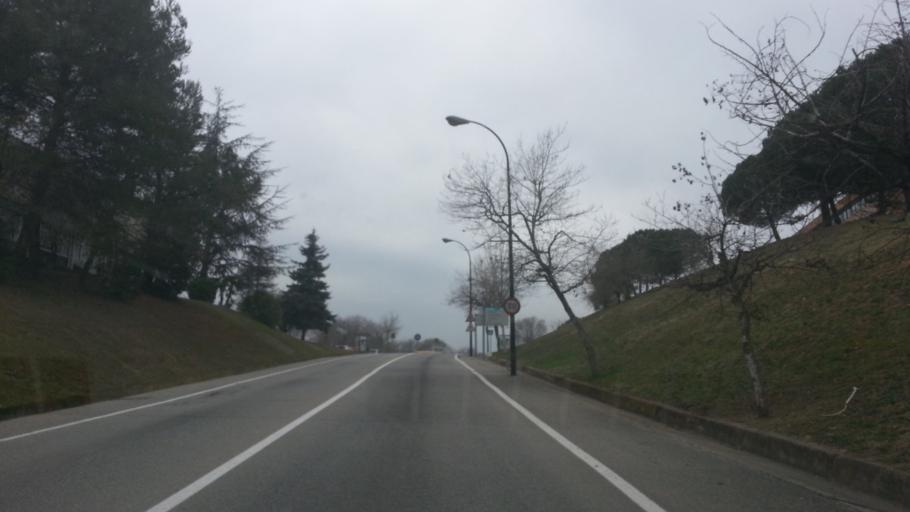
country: ES
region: Catalonia
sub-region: Provincia de Barcelona
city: Barbera del Valles
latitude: 41.5041
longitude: 2.0998
